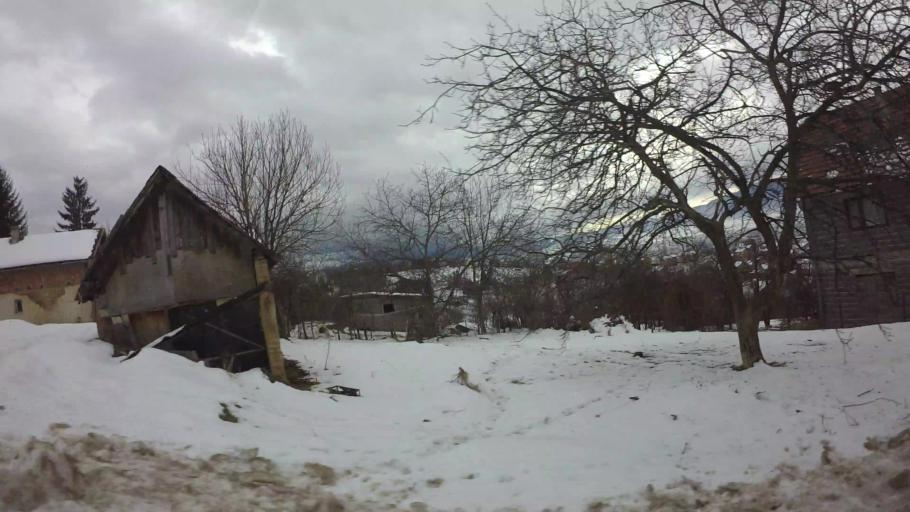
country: BA
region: Federation of Bosnia and Herzegovina
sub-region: Kanton Sarajevo
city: Sarajevo
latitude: 43.8625
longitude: 18.3348
